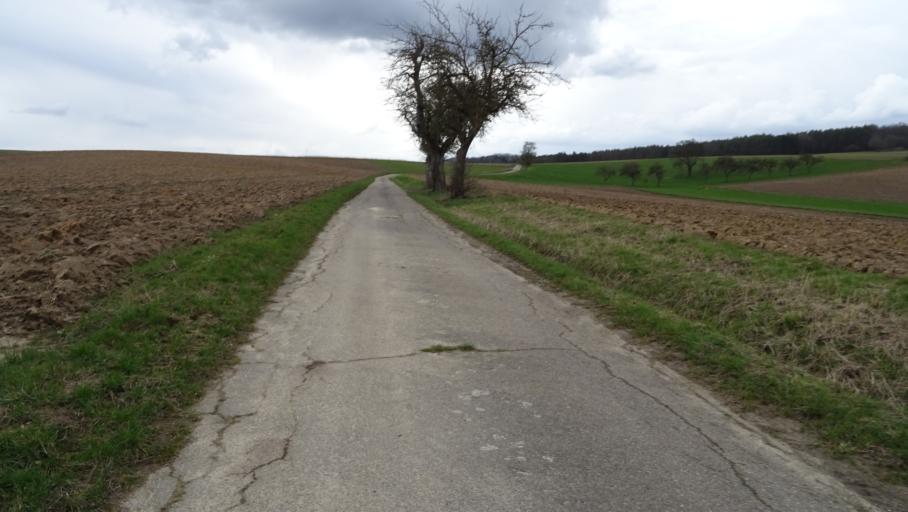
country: DE
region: Baden-Wuerttemberg
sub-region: Karlsruhe Region
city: Seckach
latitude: 49.4315
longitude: 9.2801
